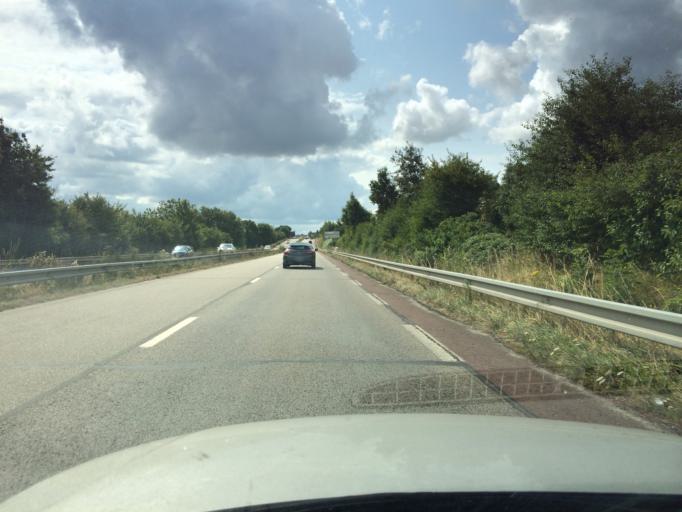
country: FR
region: Lower Normandy
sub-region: Departement de la Manche
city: Sainte-Mere-Eglise
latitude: 49.4341
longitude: -1.3375
